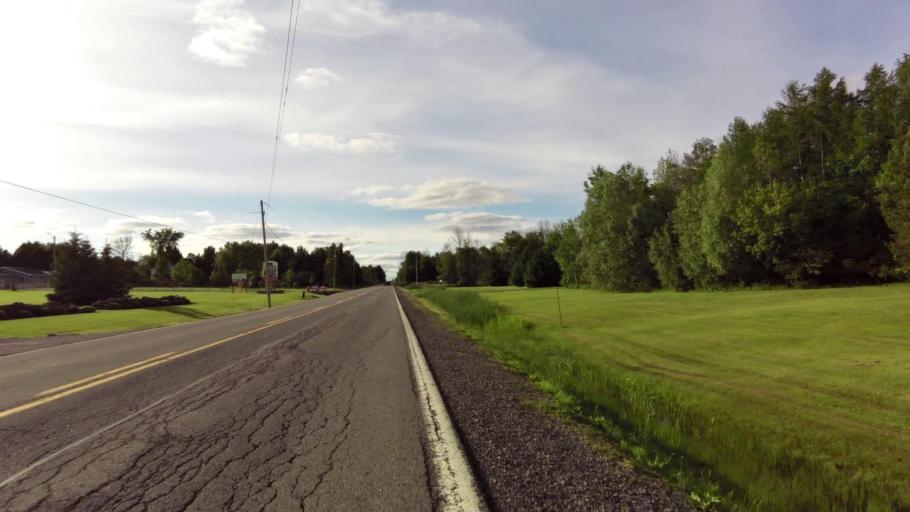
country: CA
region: Ontario
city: Ottawa
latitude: 45.2231
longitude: -75.6044
